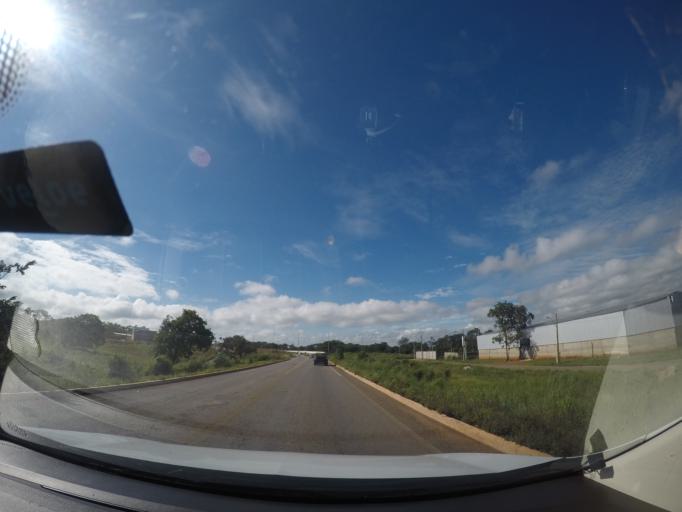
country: BR
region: Goias
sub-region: Senador Canedo
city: Senador Canedo
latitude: -16.6816
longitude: -49.1407
